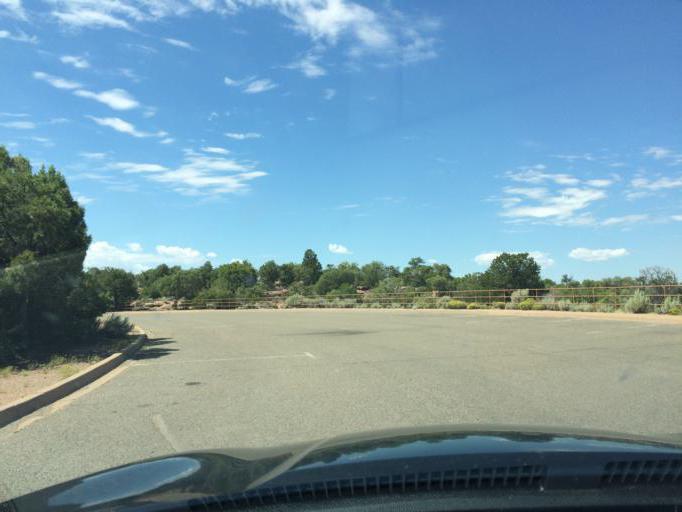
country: US
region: Arizona
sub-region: Apache County
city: Chinle
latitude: 36.1039
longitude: -109.3568
